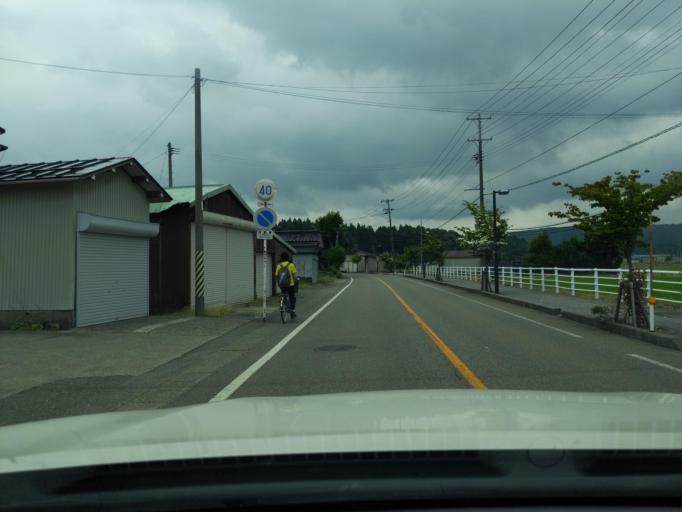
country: JP
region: Niigata
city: Kashiwazaki
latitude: 37.3387
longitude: 138.5725
